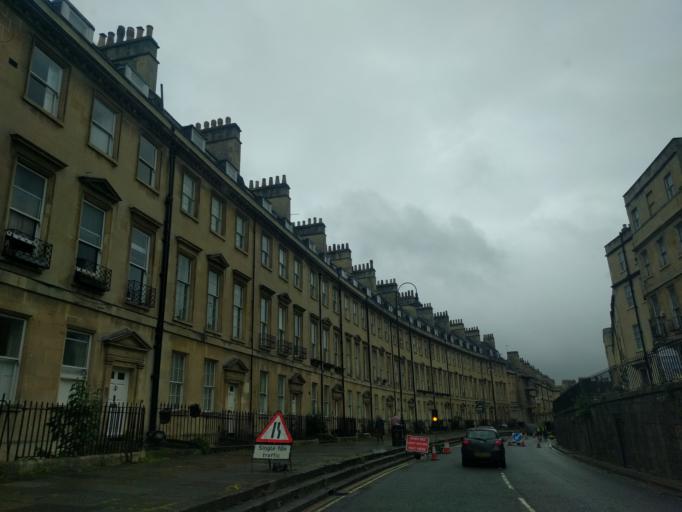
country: GB
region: England
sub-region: Bath and North East Somerset
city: Bath
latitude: 51.3869
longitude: -2.3600
